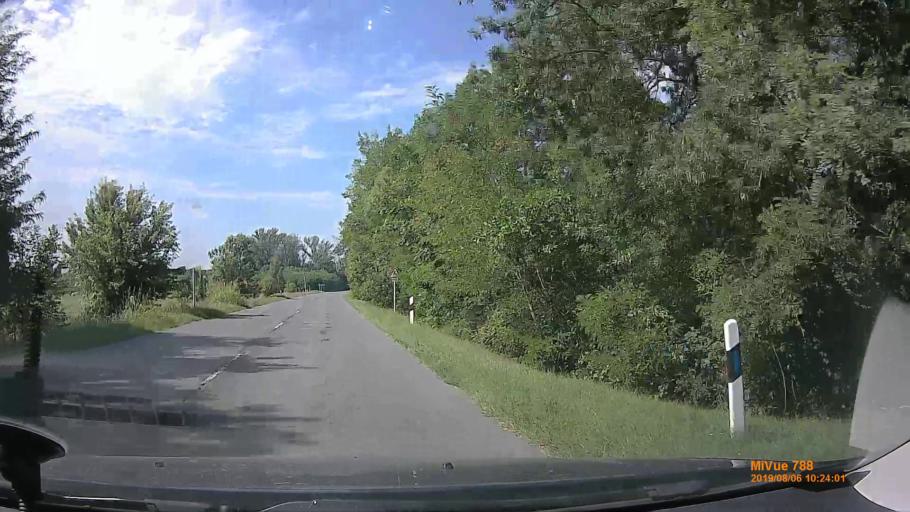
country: HU
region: Somogy
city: Balatonbereny
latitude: 46.6484
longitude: 17.3094
